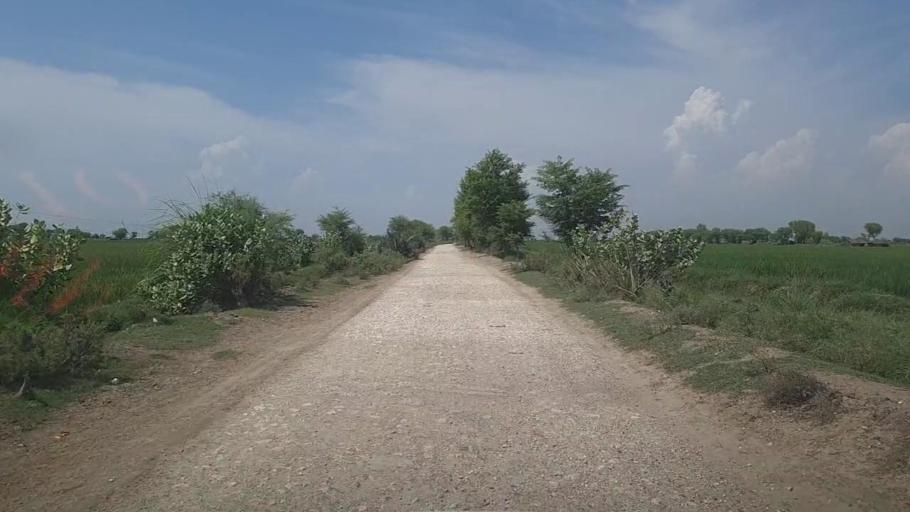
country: PK
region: Sindh
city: Kandhkot
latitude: 28.3030
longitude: 69.2442
